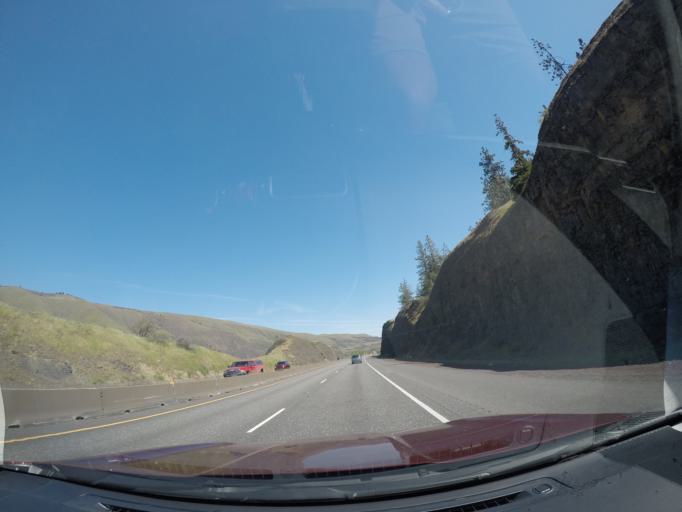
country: US
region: Oregon
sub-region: Wasco County
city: Chenoweth
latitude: 45.6687
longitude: -121.2428
